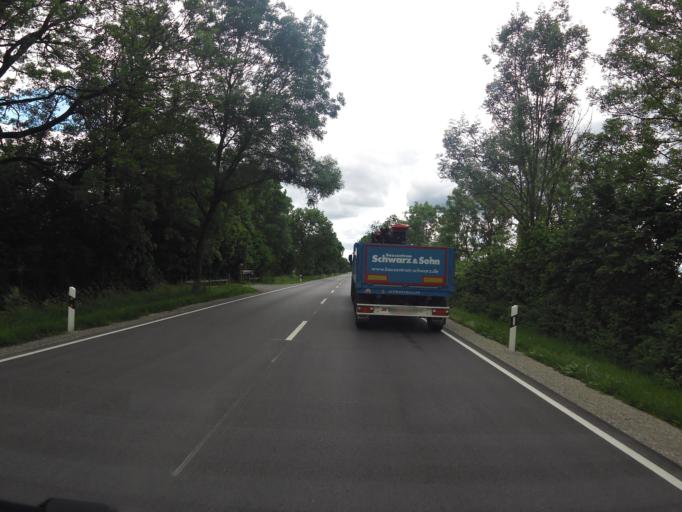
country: DE
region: Bavaria
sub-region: Upper Bavaria
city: Wang
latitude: 48.4785
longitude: 11.9823
